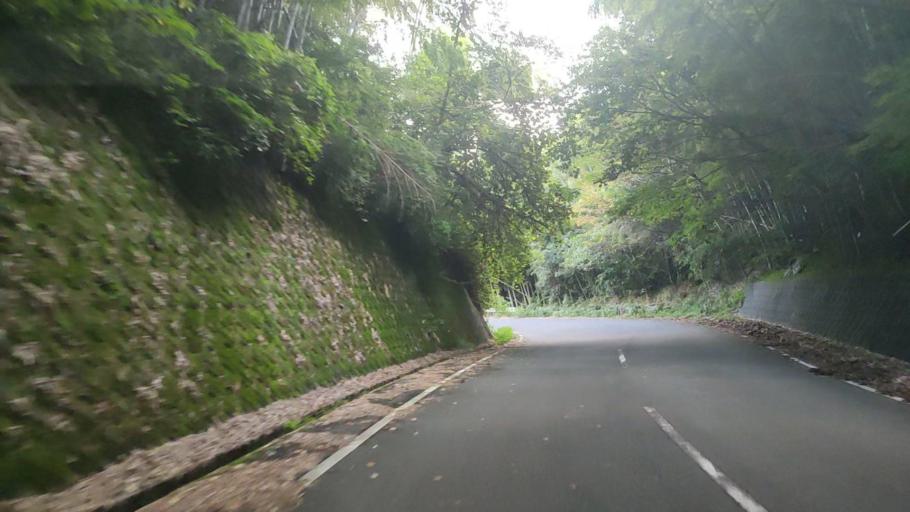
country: JP
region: Kanagawa
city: Hakone
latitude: 35.1293
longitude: 138.9886
